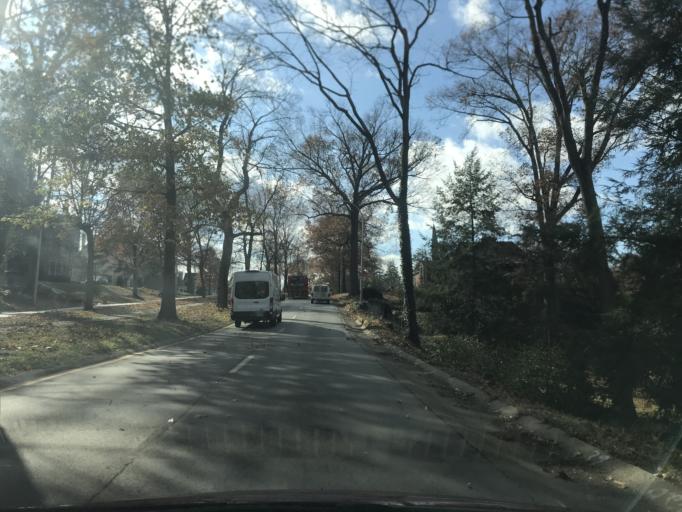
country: US
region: Kentucky
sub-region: Jefferson County
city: Audubon Park
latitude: 38.2276
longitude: -85.7183
